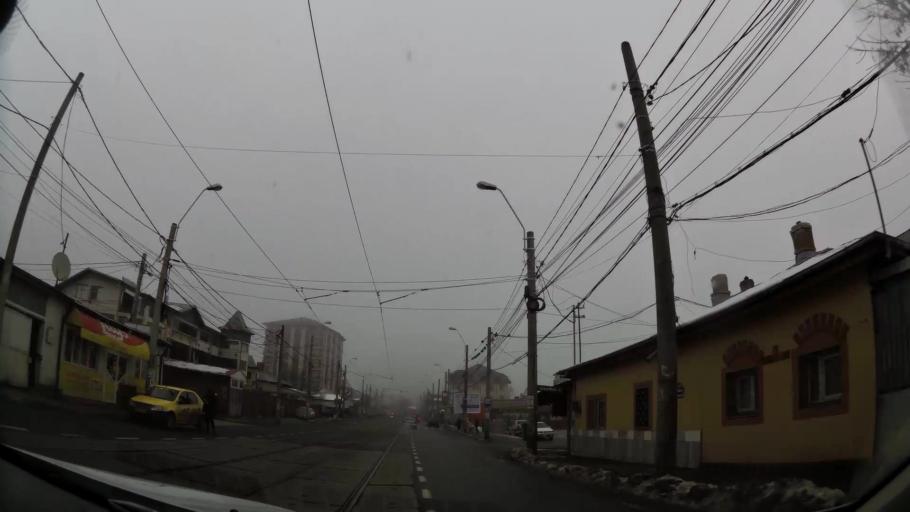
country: RO
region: Ilfov
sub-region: Comuna Chiajna
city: Rosu
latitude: 44.4666
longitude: 26.0345
